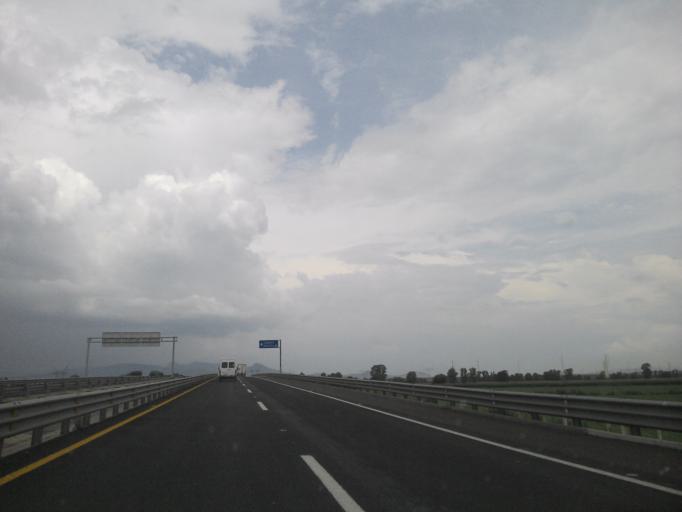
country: MX
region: Hidalgo
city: Doxey
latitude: 20.0979
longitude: -99.2780
